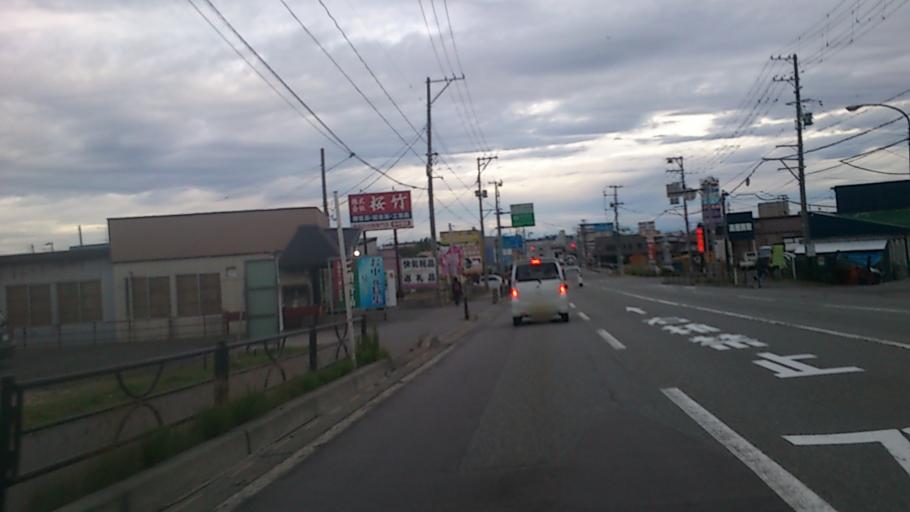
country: JP
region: Akita
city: Akita Shi
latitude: 39.7442
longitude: 140.0898
